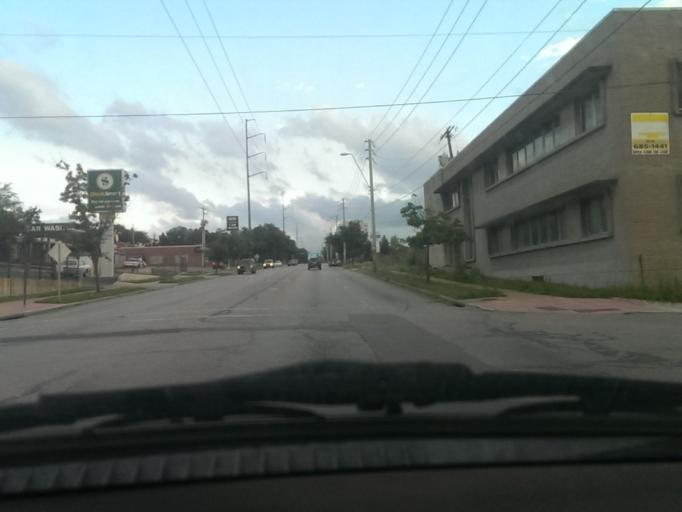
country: US
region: Kansas
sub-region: Johnson County
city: Mission Hills
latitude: 39.0099
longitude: -94.5748
